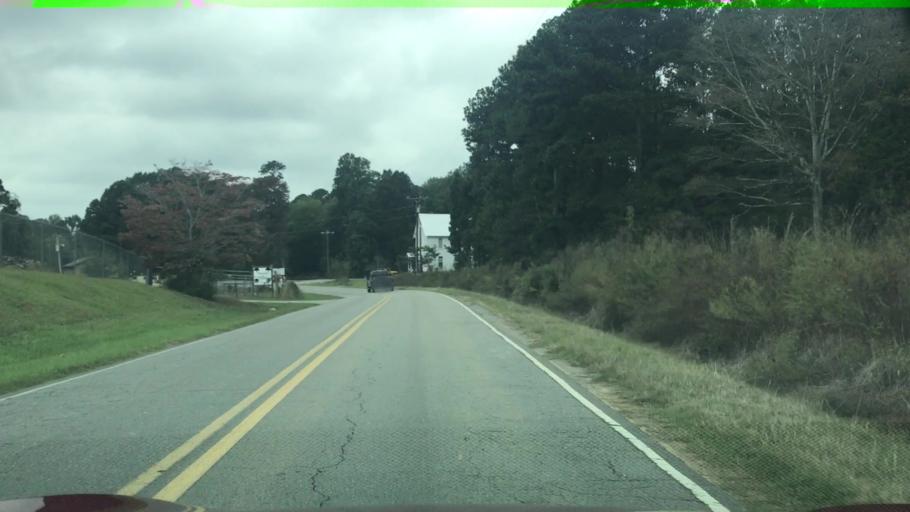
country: US
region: Alabama
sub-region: Cullman County
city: Good Hope
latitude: 34.0969
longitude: -87.0529
